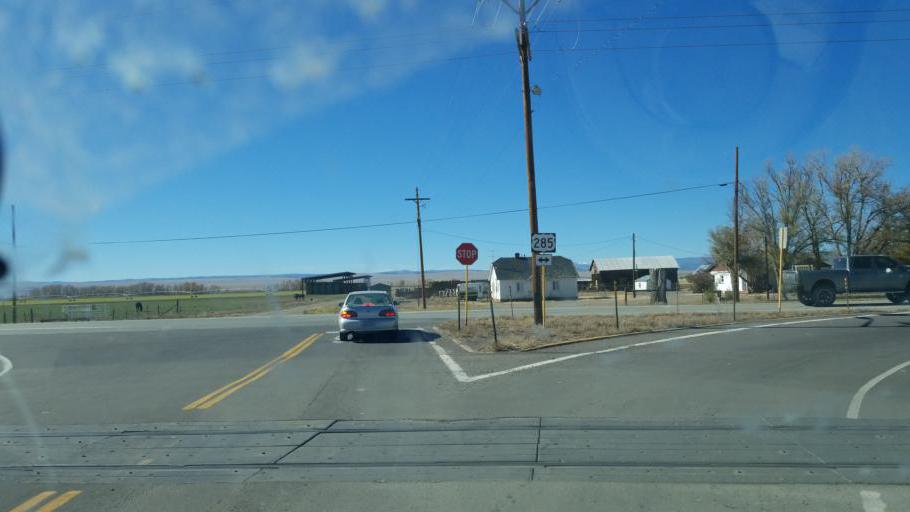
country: US
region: Colorado
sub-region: Conejos County
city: Conejos
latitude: 37.1743
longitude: -105.9874
